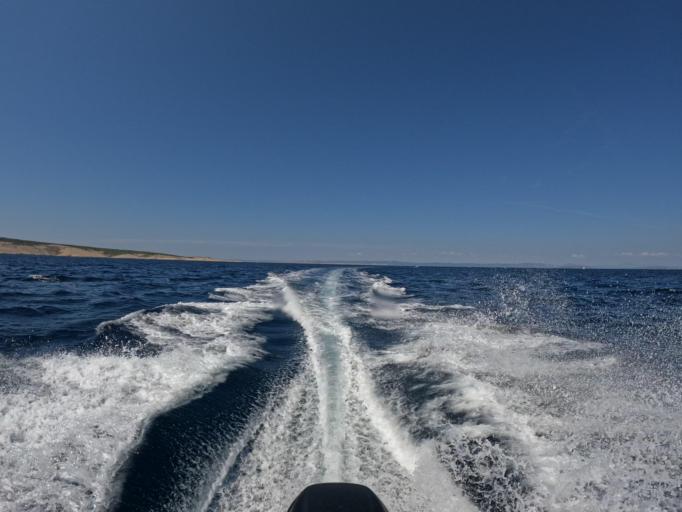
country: HR
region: Primorsko-Goranska
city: Lopar
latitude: 44.8540
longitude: 14.7132
